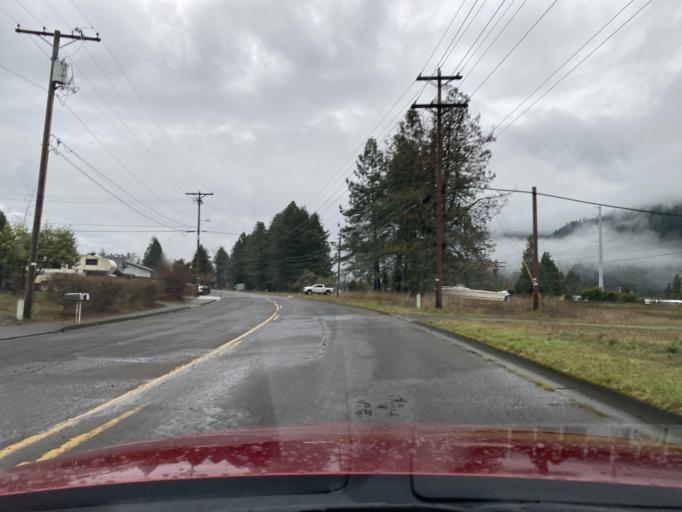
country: US
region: Oregon
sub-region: Lane County
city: Oakridge
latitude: 43.7491
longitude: -122.4819
